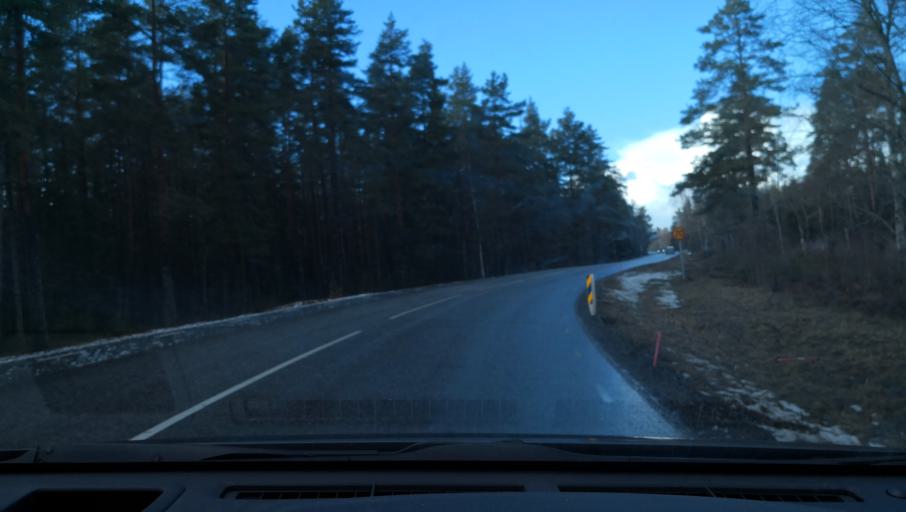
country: SE
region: Vaestmanland
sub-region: Arboga Kommun
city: Arboga
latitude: 59.3643
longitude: 15.8468
